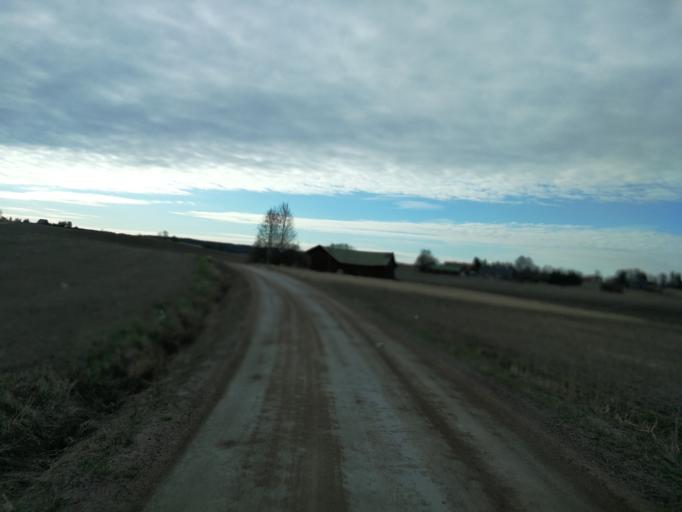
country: FI
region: Varsinais-Suomi
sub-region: Salo
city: Muurla
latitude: 60.3427
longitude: 23.2542
